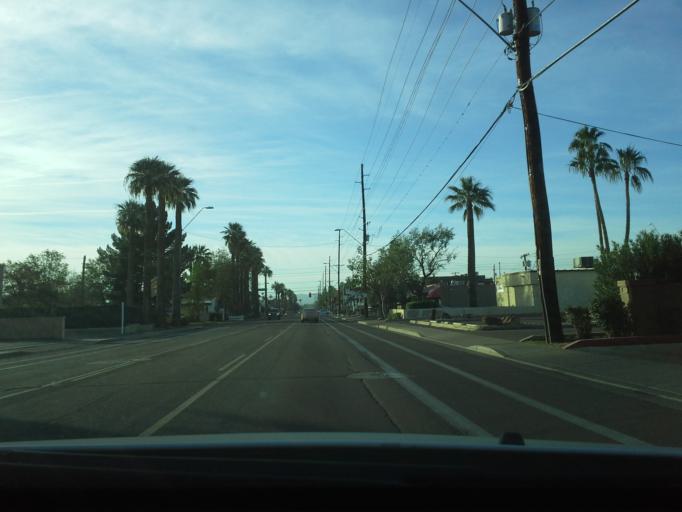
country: US
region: Arizona
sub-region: Maricopa County
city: Phoenix
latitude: 33.5073
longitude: -112.0563
